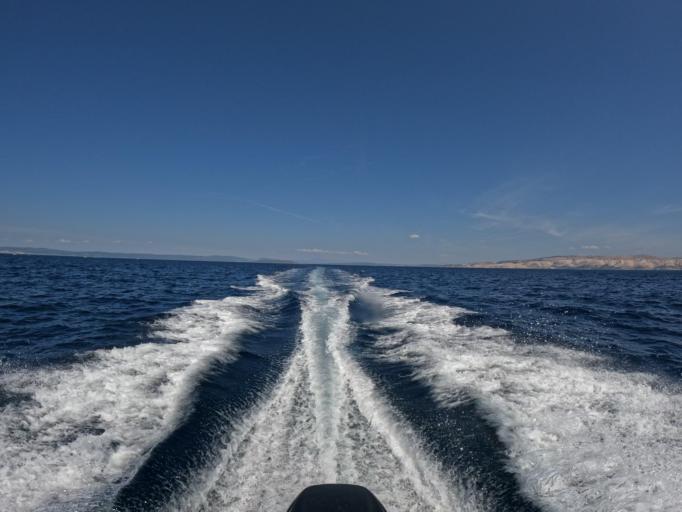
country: HR
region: Primorsko-Goranska
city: Lopar
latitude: 44.8794
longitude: 14.6590
